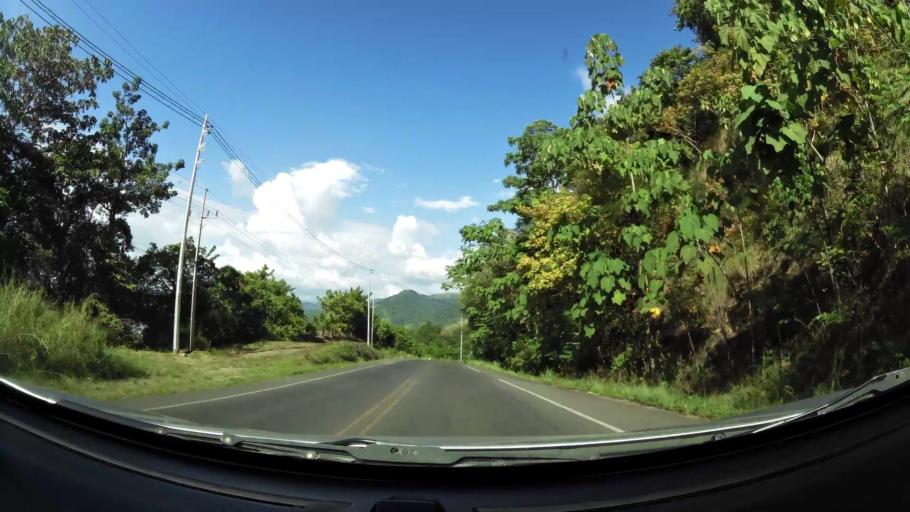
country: CR
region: Puntarenas
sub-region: Canton de Garabito
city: Jaco
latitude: 9.5950
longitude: -84.6208
